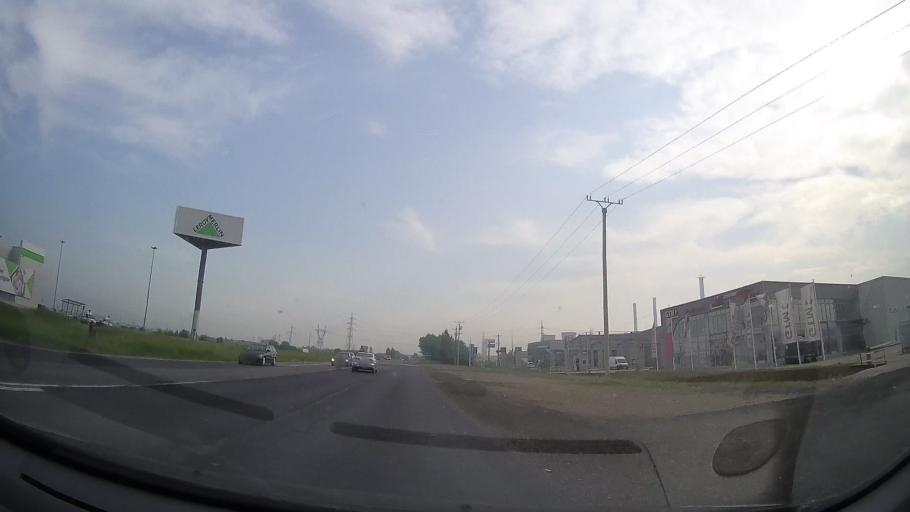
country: RO
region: Timis
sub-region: Comuna Giroc
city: Chisoda
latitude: 45.7029
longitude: 21.1842
